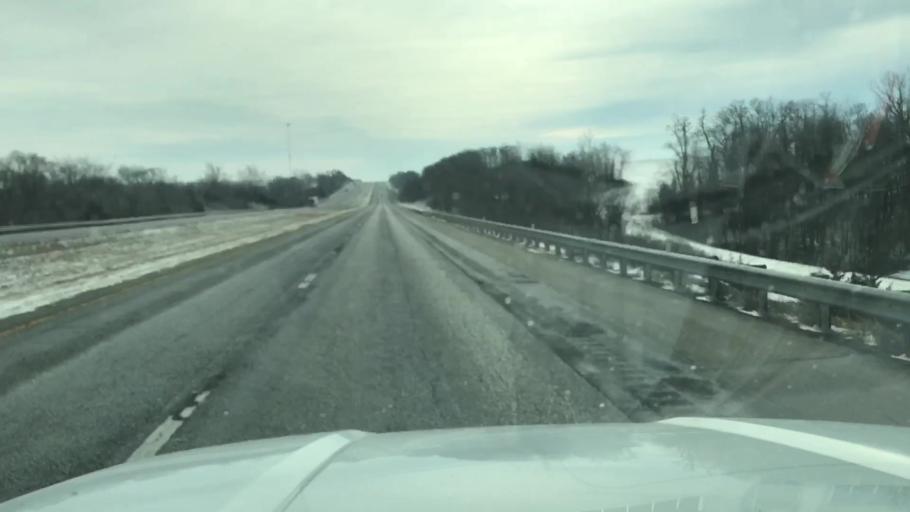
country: US
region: Missouri
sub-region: Holt County
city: Oregon
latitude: 40.0094
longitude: -95.0767
